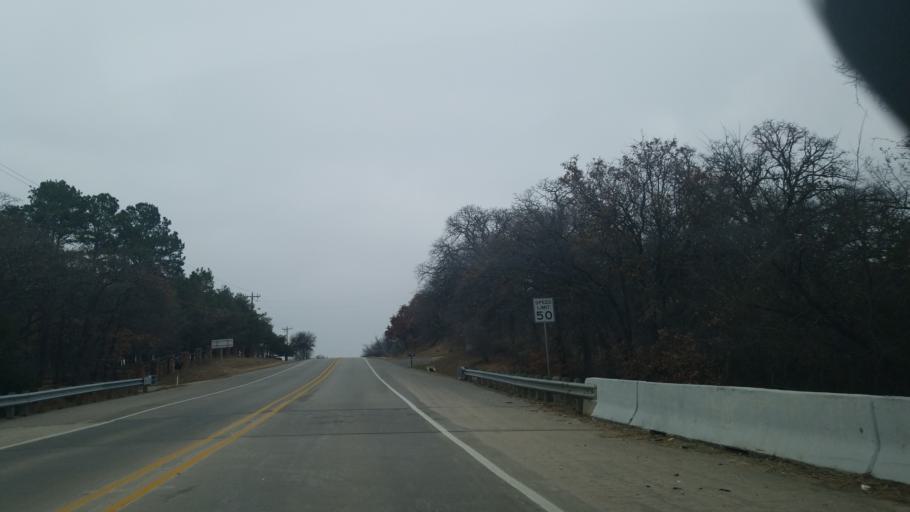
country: US
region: Texas
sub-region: Denton County
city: Bartonville
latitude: 33.1068
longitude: -97.1398
